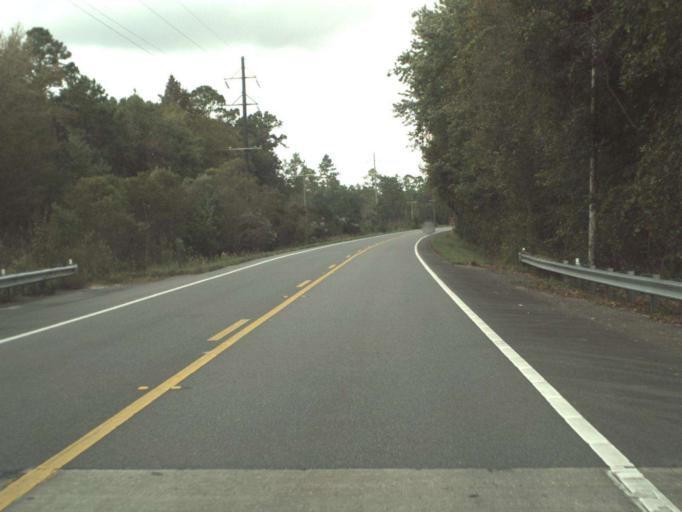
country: US
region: Florida
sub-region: Franklin County
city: Carrabelle
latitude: 29.9950
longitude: -84.5037
